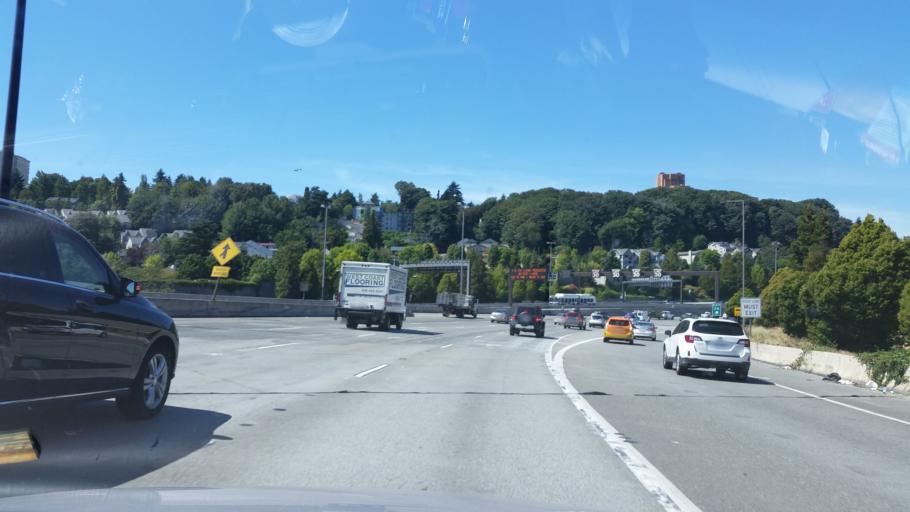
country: US
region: Washington
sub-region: King County
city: Seattle
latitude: 47.5906
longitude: -122.3078
